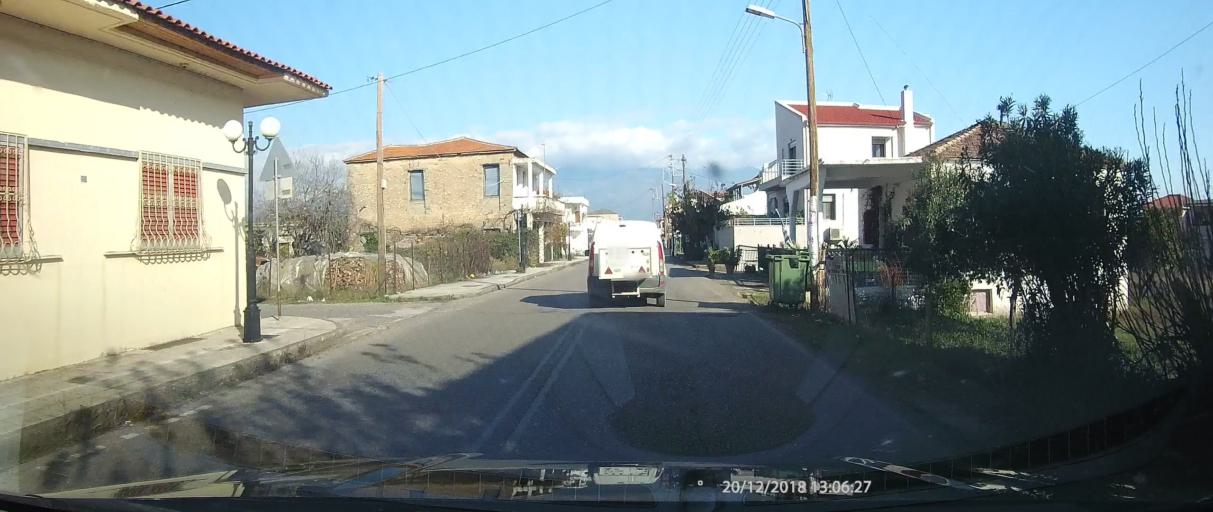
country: GR
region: West Greece
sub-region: Nomos Aitolias kai Akarnanias
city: Panaitolion
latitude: 38.5832
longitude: 21.4486
